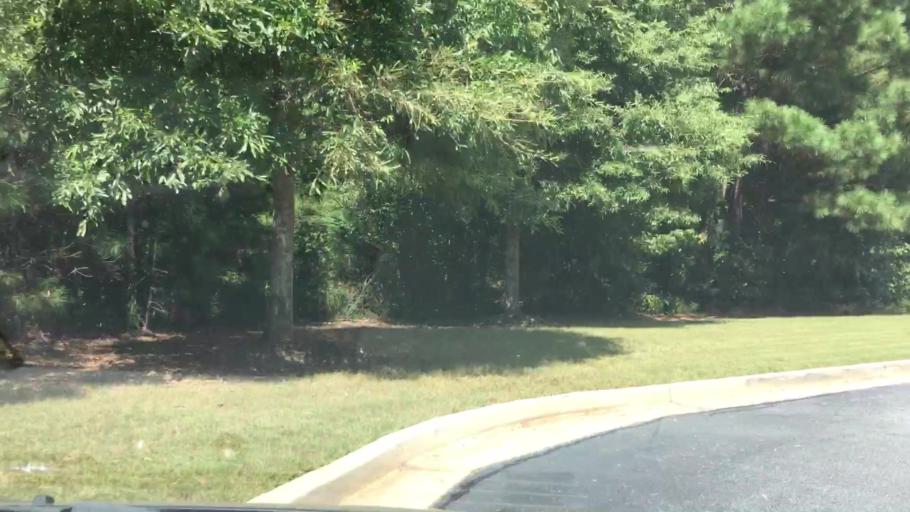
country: US
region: Georgia
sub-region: Henry County
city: Stockbridge
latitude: 33.5142
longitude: -84.2150
